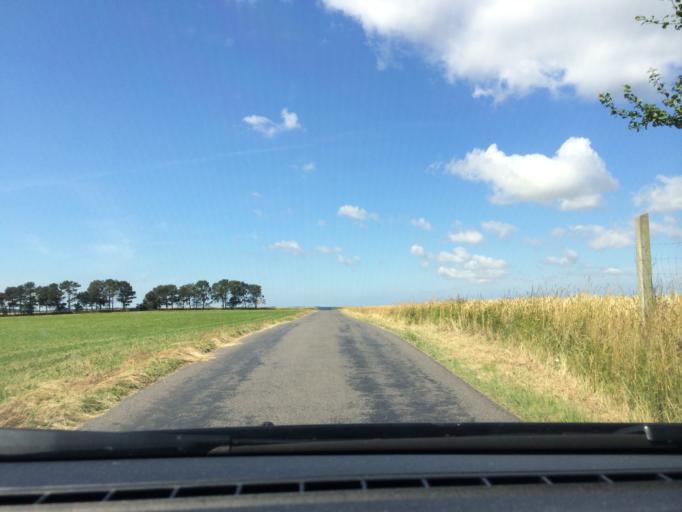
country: DK
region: Zealand
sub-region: Vordingborg Kommune
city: Stege
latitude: 55.0448
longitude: 12.1957
